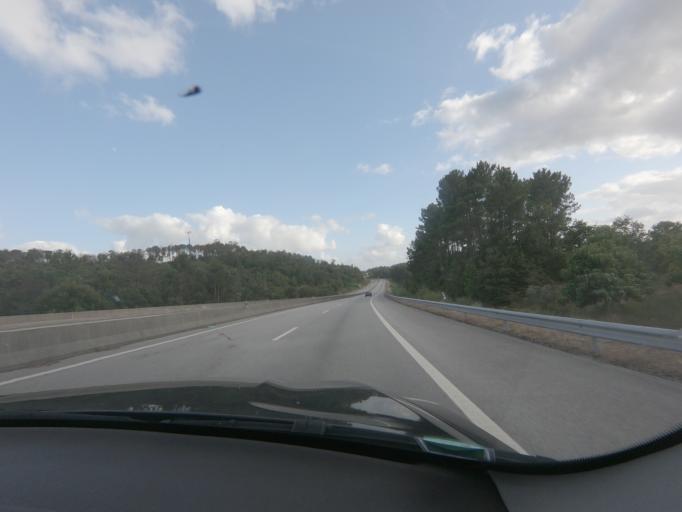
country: PT
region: Viseu
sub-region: Viseu
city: Abraveses
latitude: 40.6553
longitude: -7.9667
